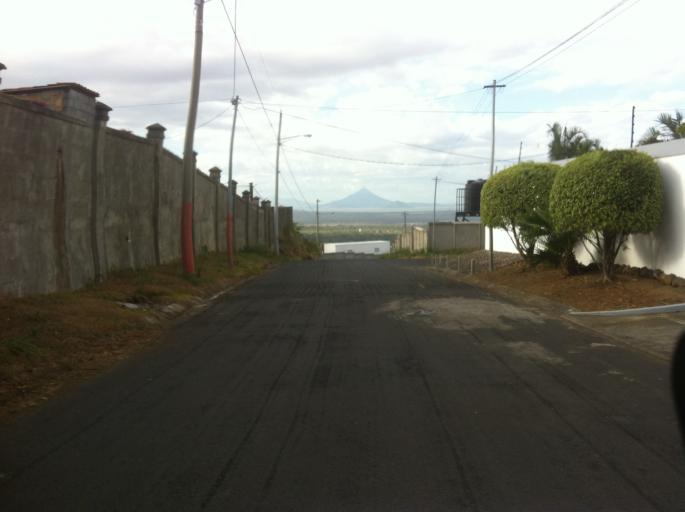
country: NI
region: Managua
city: Ciudad Sandino
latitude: 12.1011
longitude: -86.3282
